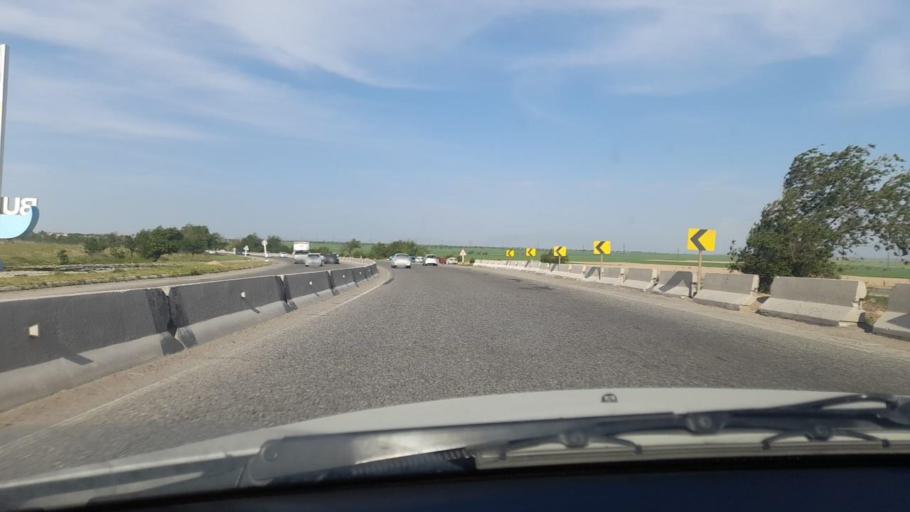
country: UZ
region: Samarqand
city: Bulung'ur
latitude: 39.8364
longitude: 67.4426
